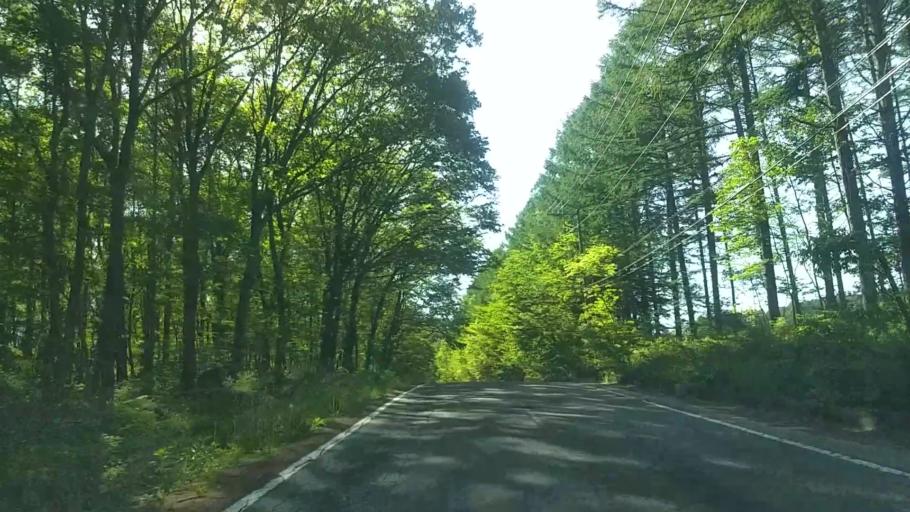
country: JP
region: Yamanashi
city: Nirasaki
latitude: 35.8893
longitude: 138.3557
